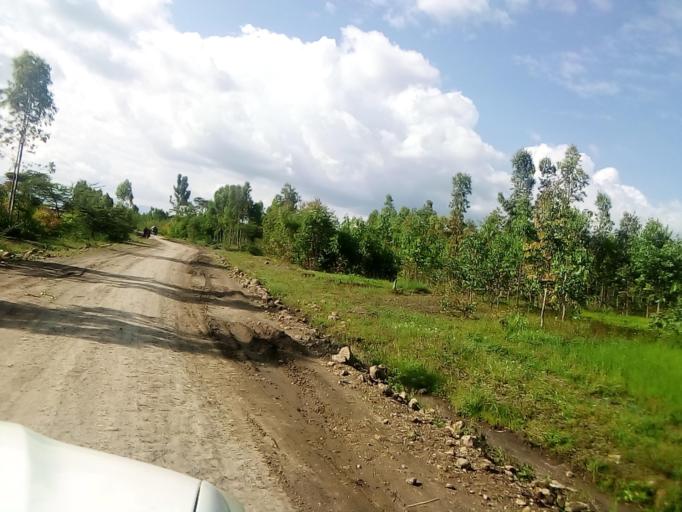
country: ET
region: Southern Nations, Nationalities, and People's Region
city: K'olito
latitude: 7.6517
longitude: 38.0504
